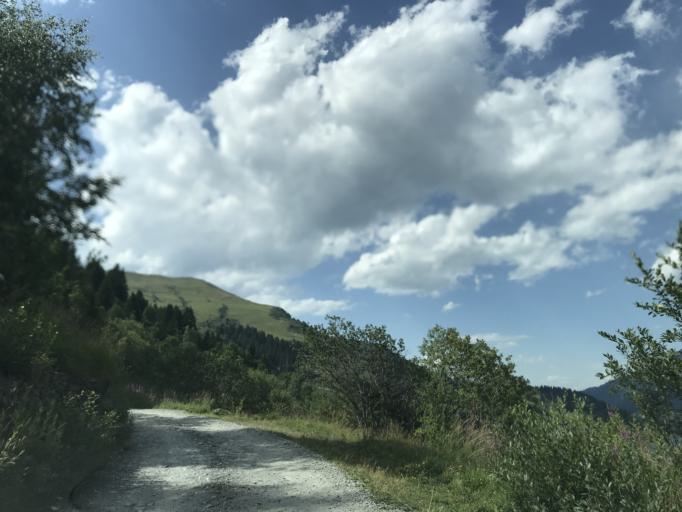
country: FR
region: Rhone-Alpes
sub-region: Departement de la Savoie
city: Beaufort
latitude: 45.6629
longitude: 6.6213
